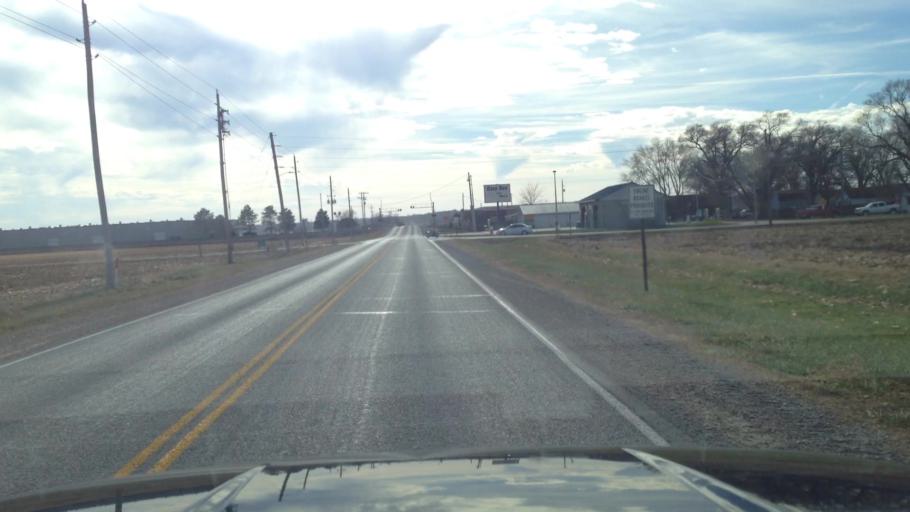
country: US
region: Kansas
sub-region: Jefferson County
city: Oskaloosa
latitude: 39.0740
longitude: -95.3820
